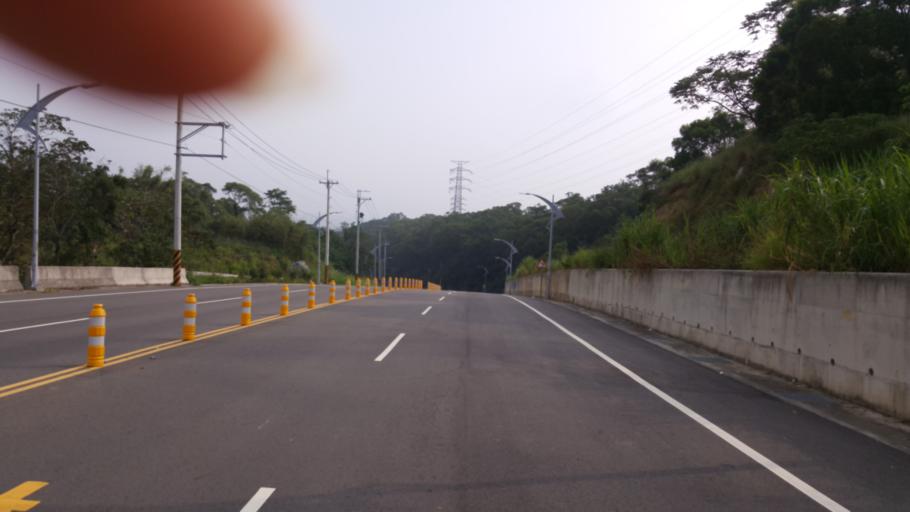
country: TW
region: Taiwan
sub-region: Hsinchu
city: Hsinchu
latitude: 24.7461
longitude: 120.9578
